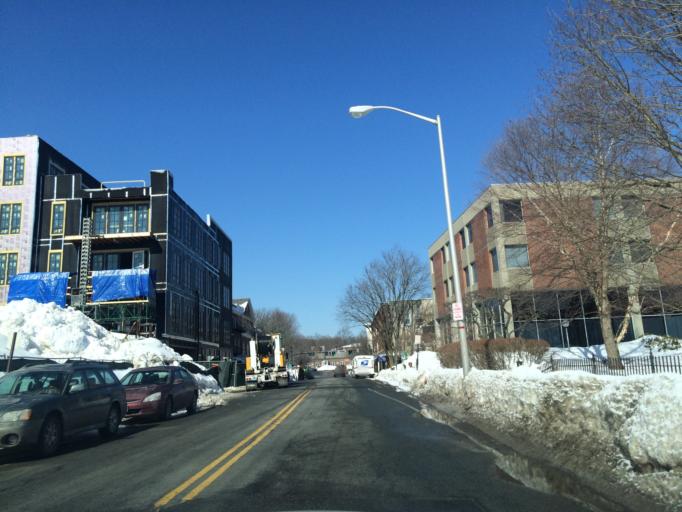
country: US
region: Massachusetts
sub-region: Norfolk County
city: Wellesley
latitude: 42.2953
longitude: -71.2920
